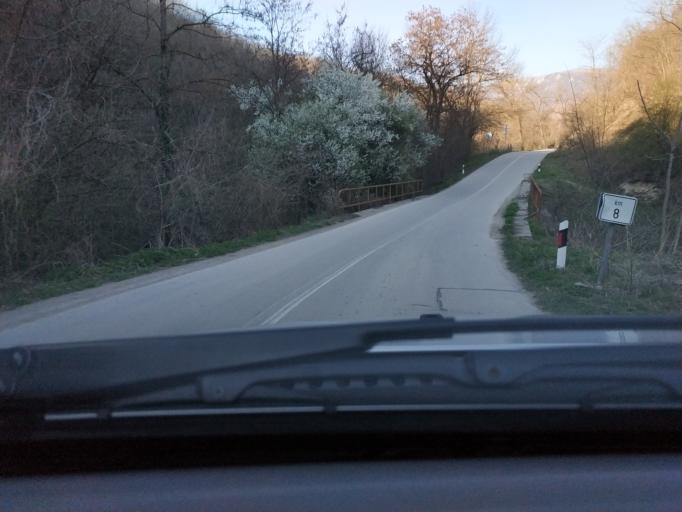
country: RS
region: Central Serbia
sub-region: Nisavski Okrug
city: Aleksinac
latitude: 43.5424
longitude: 21.8061
